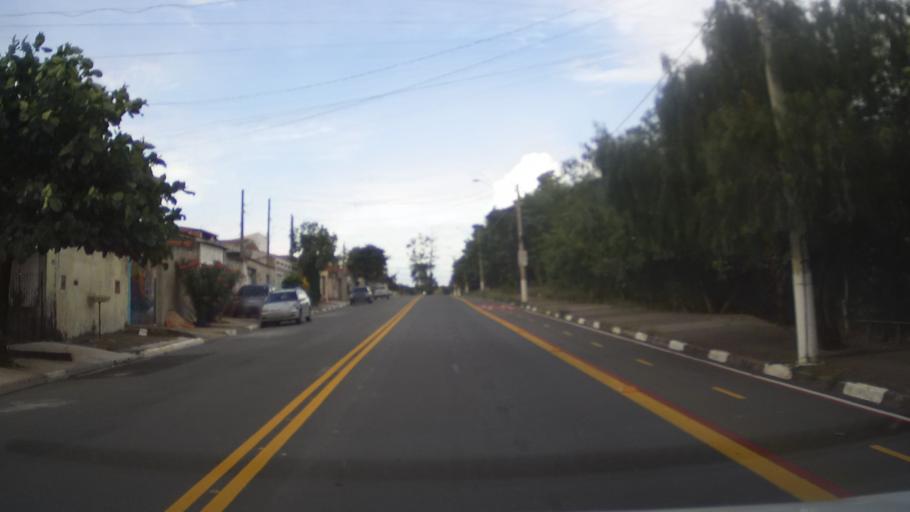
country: BR
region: Sao Paulo
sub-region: Hortolandia
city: Hortolandia
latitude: -22.9559
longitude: -47.1951
